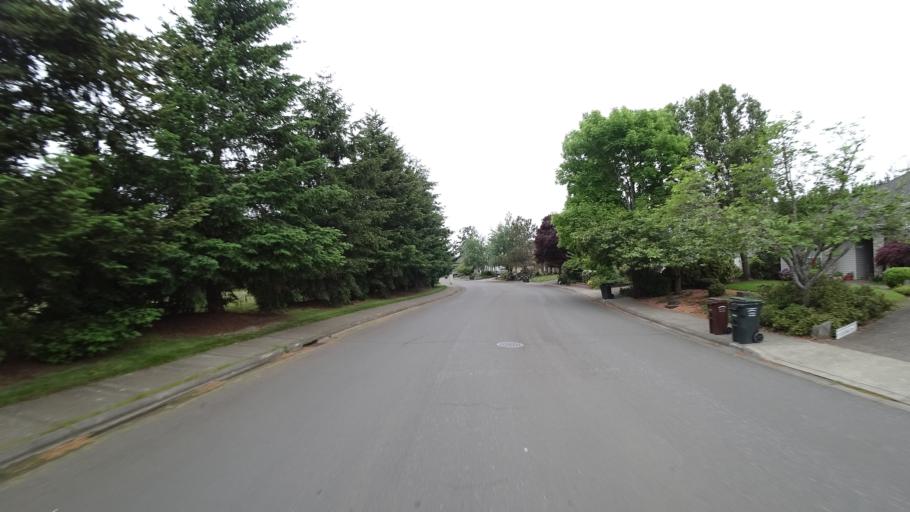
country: US
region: Oregon
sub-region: Washington County
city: Bethany
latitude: 45.5463
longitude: -122.8567
